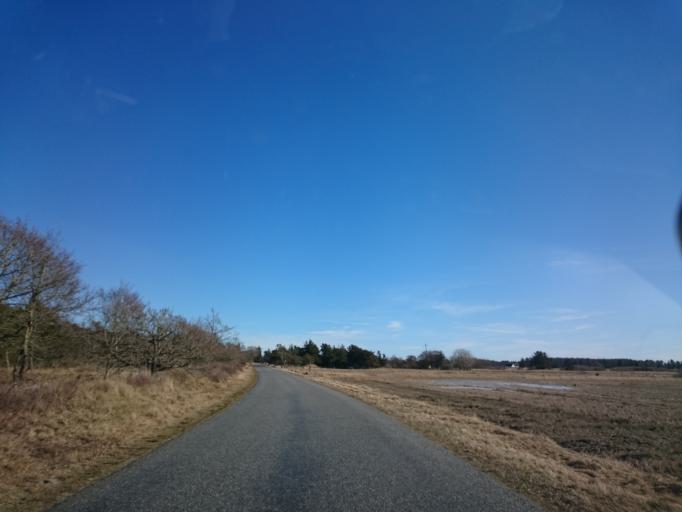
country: DK
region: North Denmark
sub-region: Frederikshavn Kommune
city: Strandby
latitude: 57.6255
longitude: 10.3744
